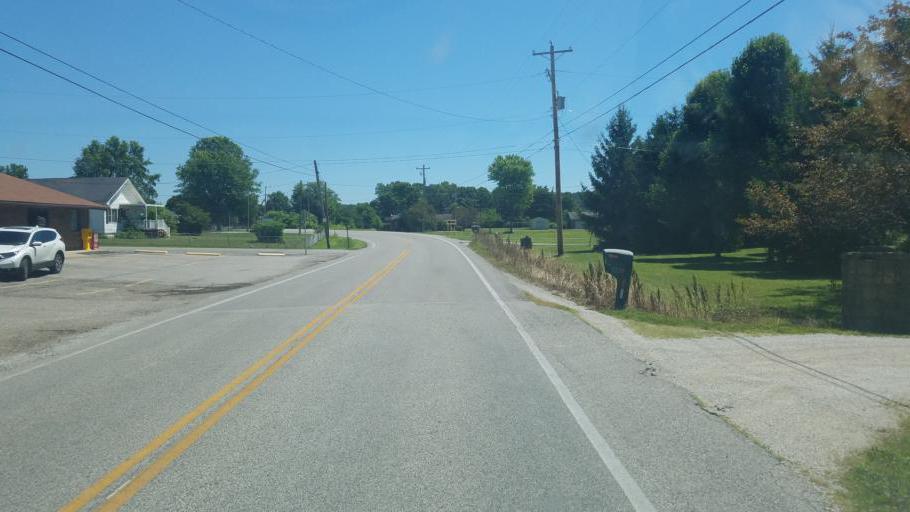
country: US
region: West Virginia
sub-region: Cabell County
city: Pea Ridge
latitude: 38.4449
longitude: -82.3348
